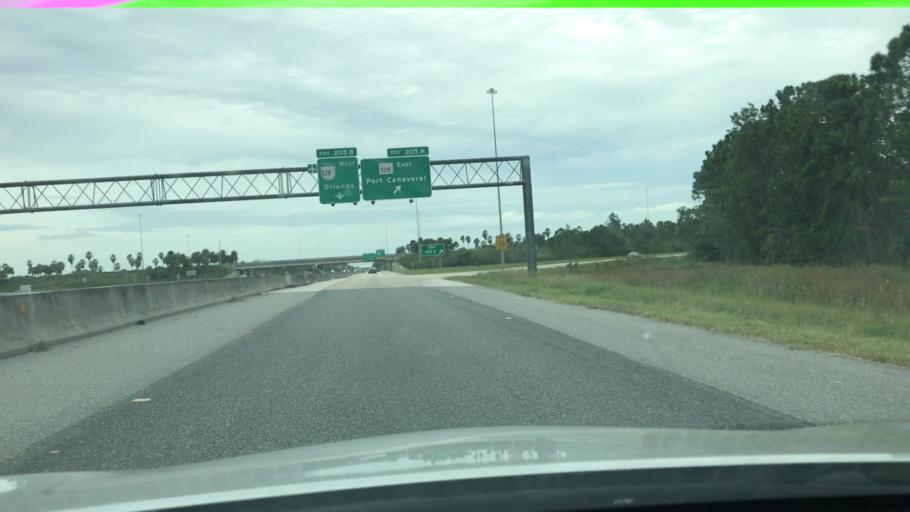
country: US
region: Florida
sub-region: Brevard County
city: Sharpes
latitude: 28.4077
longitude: -80.8201
